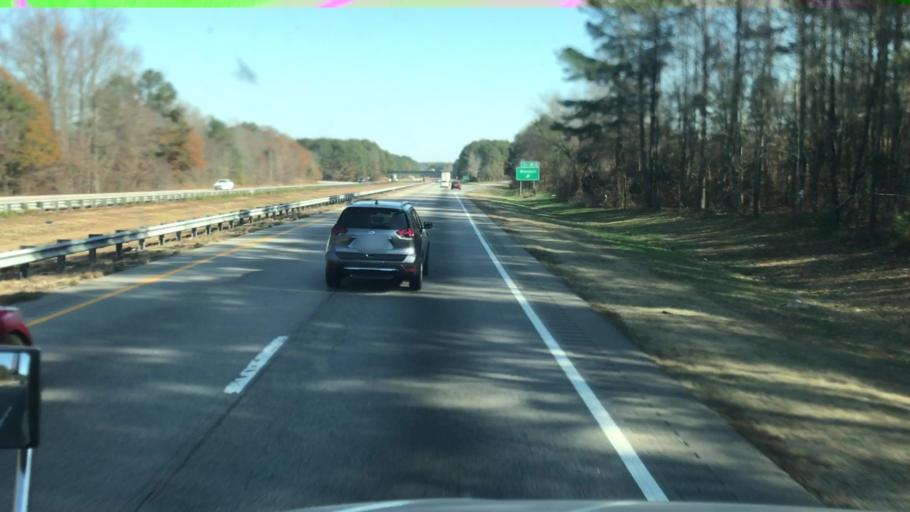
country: US
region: North Carolina
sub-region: Wake County
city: Wendell
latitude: 35.8234
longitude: -78.3812
